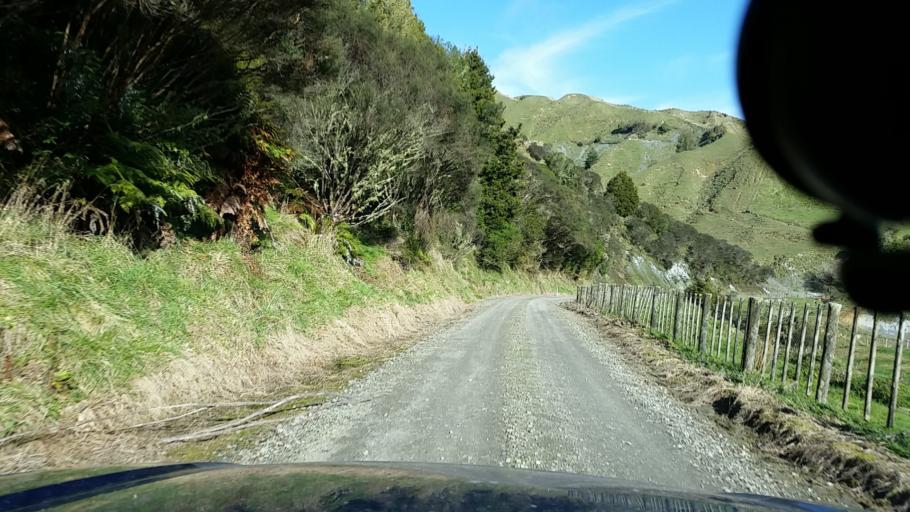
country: NZ
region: Taranaki
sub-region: New Plymouth District
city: Waitara
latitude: -39.0516
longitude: 174.7552
